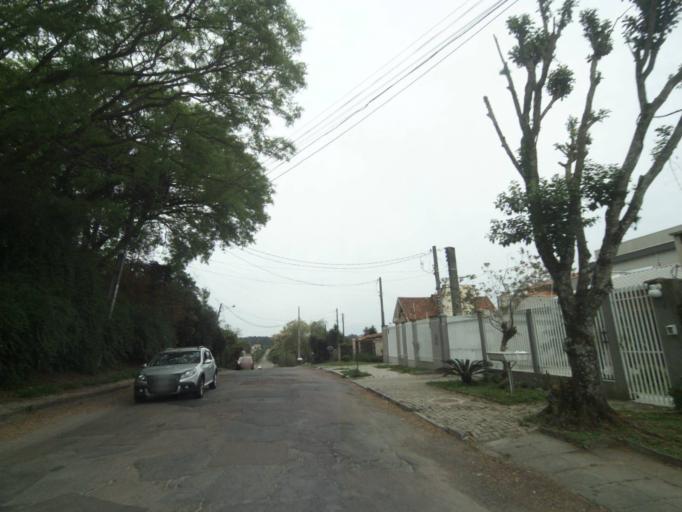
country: BR
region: Parana
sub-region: Pinhais
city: Pinhais
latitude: -25.4193
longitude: -49.2116
